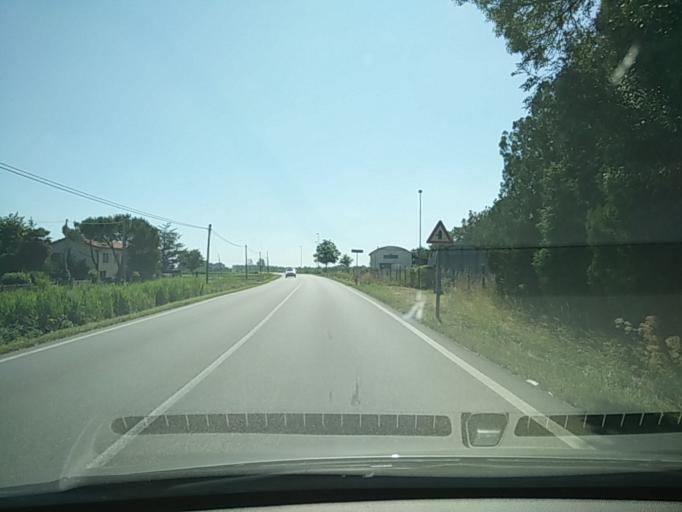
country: IT
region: Veneto
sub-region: Provincia di Venezia
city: Ceggia
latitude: 45.6360
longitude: 12.6385
